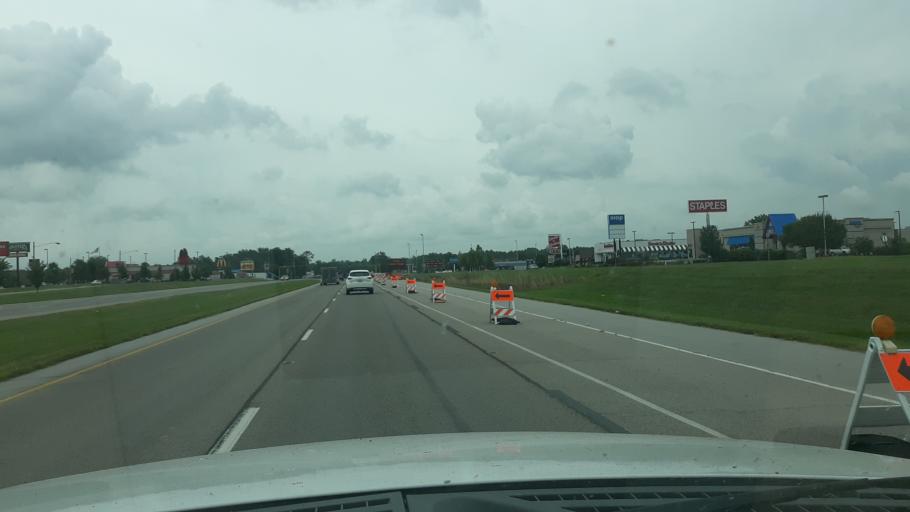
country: US
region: Illinois
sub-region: Jackson County
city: Carbondale
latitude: 37.7330
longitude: -89.1897
